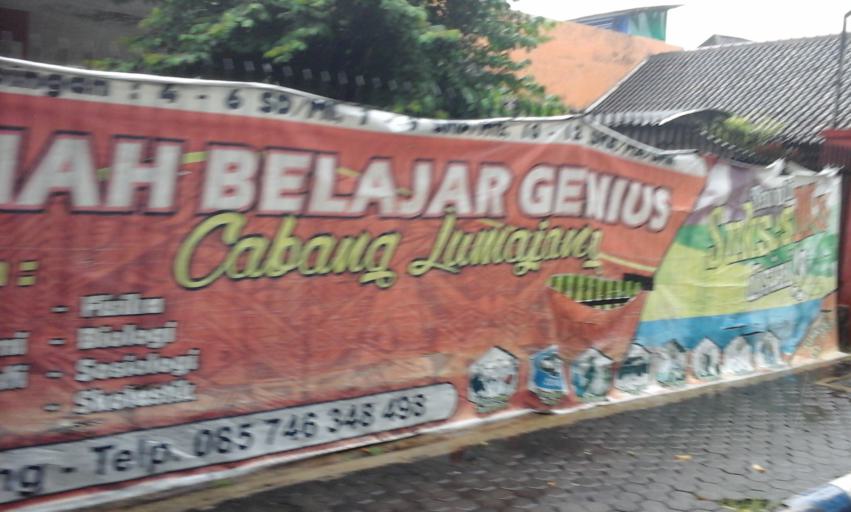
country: ID
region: East Java
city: Lumajang
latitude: -8.1345
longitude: 113.2263
